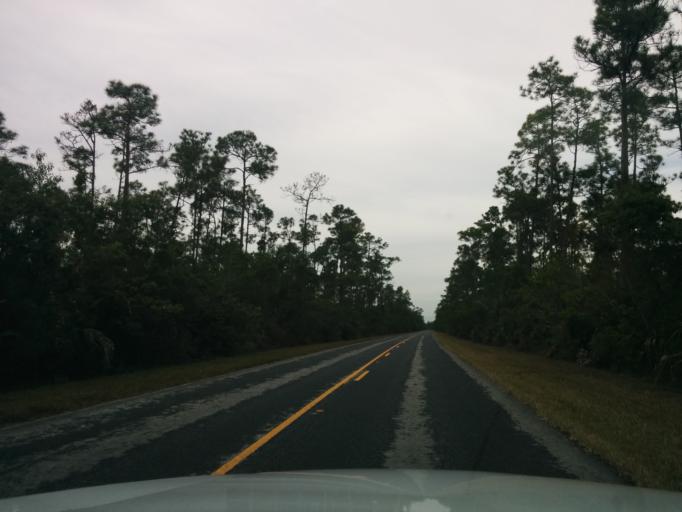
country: US
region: Florida
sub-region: Miami-Dade County
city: Florida City
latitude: 25.4251
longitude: -80.6829
